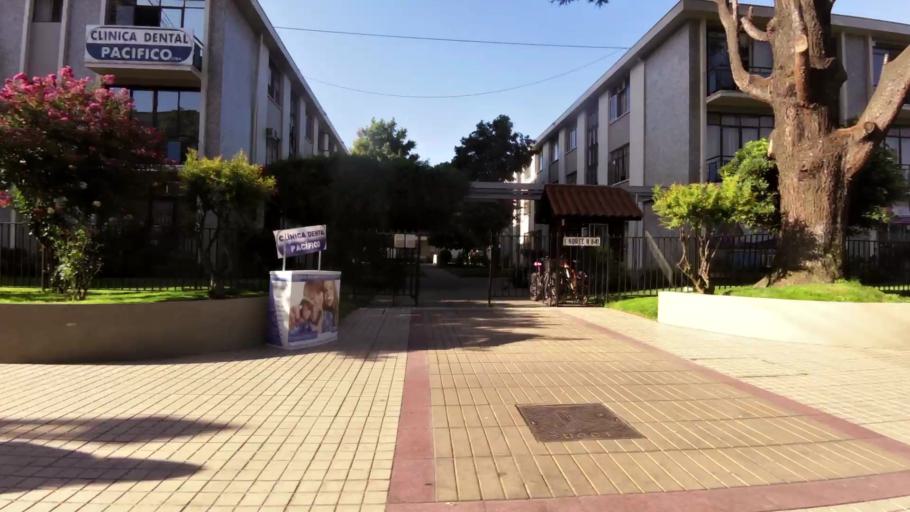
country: CL
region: Maule
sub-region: Provincia de Talca
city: Talca
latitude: -35.4261
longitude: -71.6646
